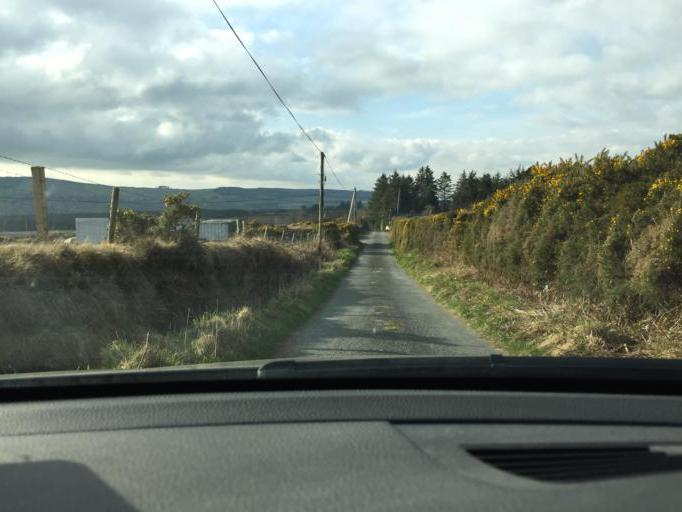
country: IE
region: Leinster
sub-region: Wicklow
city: Valleymount
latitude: 53.0801
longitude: -6.5134
